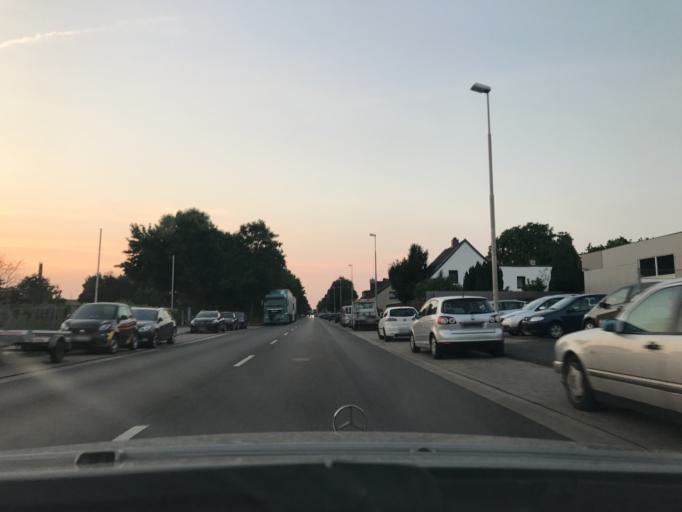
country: DE
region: North Rhine-Westphalia
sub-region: Regierungsbezirk Dusseldorf
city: Willich
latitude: 51.2765
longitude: 6.5549
